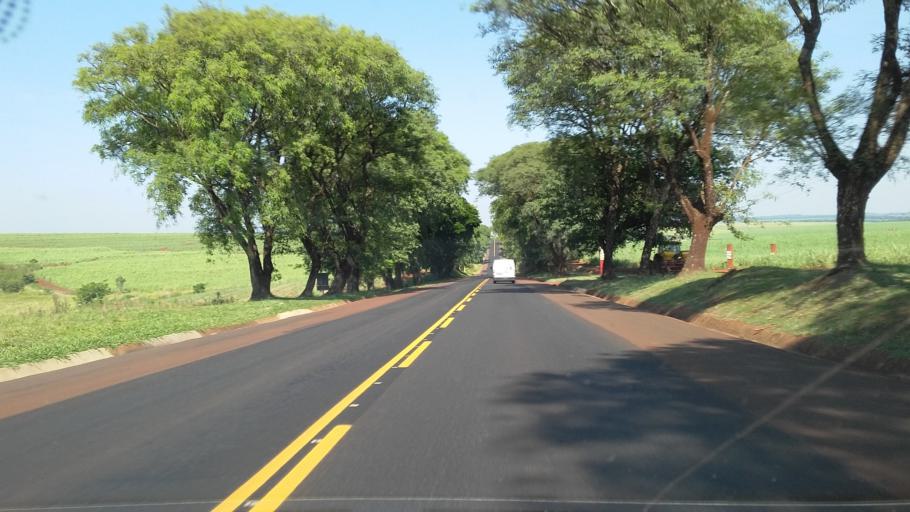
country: BR
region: Parana
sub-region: Bandeirantes
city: Bandeirantes
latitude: -23.1325
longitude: -50.4305
